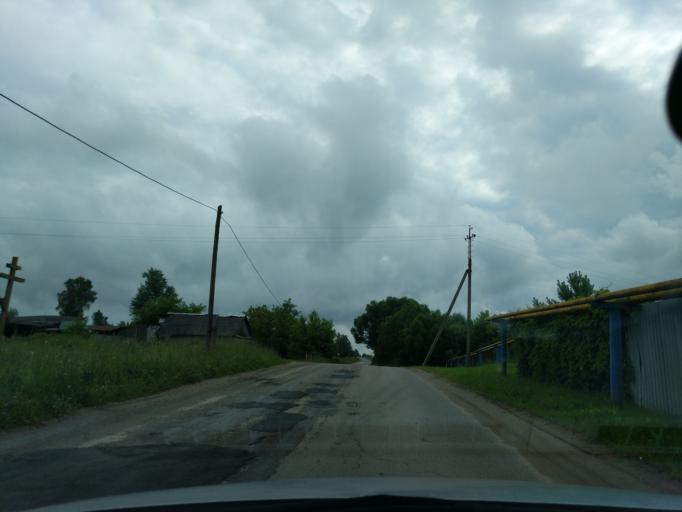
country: RU
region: Kaluga
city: Myatlevo
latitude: 54.7984
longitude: 35.7405
